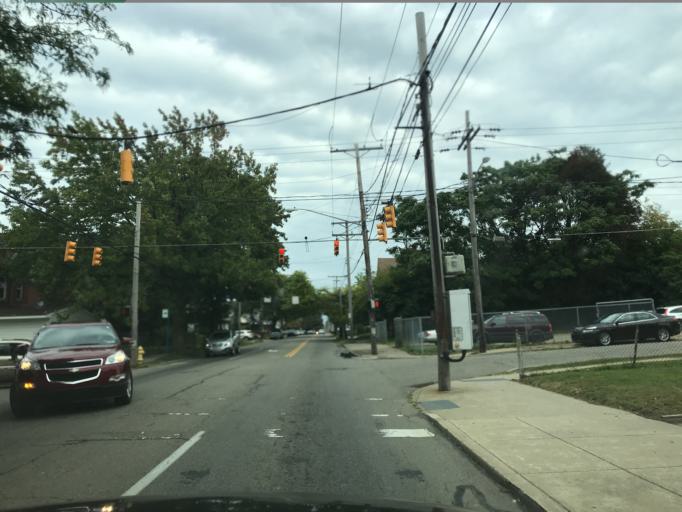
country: US
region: Pennsylvania
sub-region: Erie County
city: Erie
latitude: 42.1182
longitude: -80.0561
